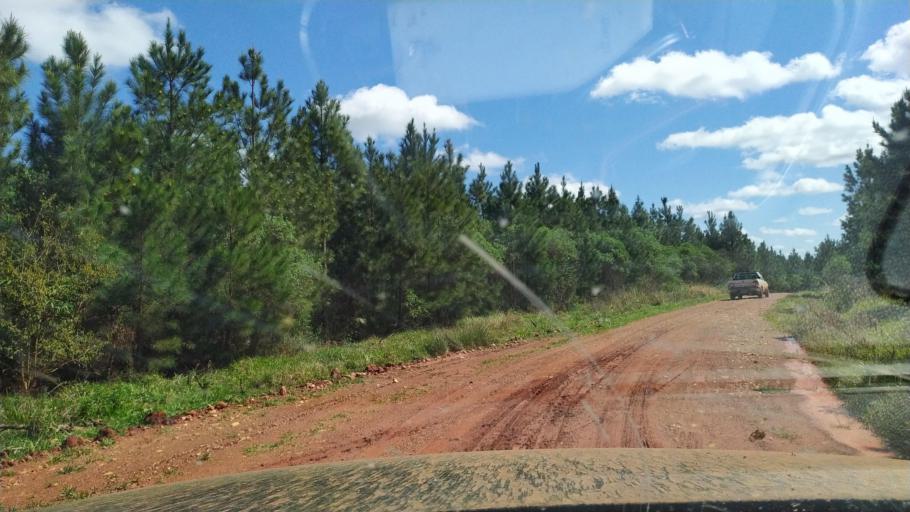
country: AR
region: Corrientes
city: Santo Tome
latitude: -28.4674
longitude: -55.9811
